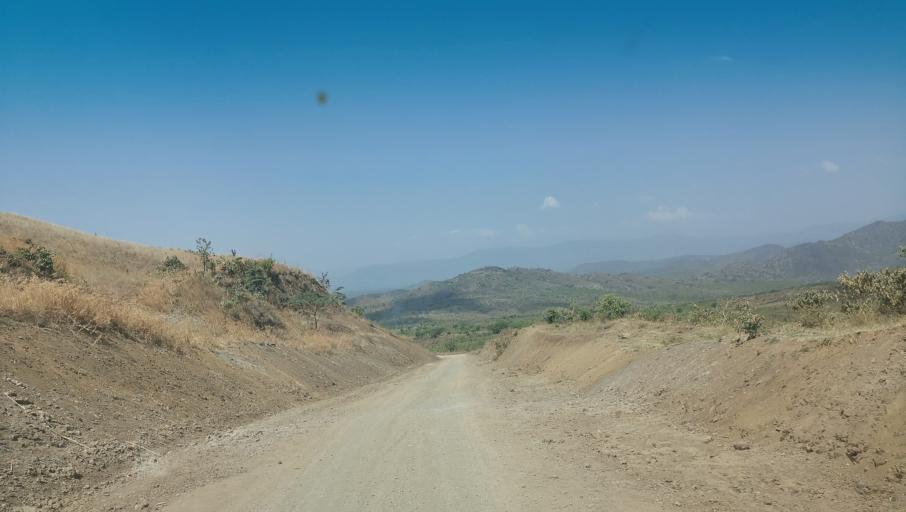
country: ET
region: Southern Nations, Nationalities, and People's Region
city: Arba Minch'
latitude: 6.3328
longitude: 37.3325
